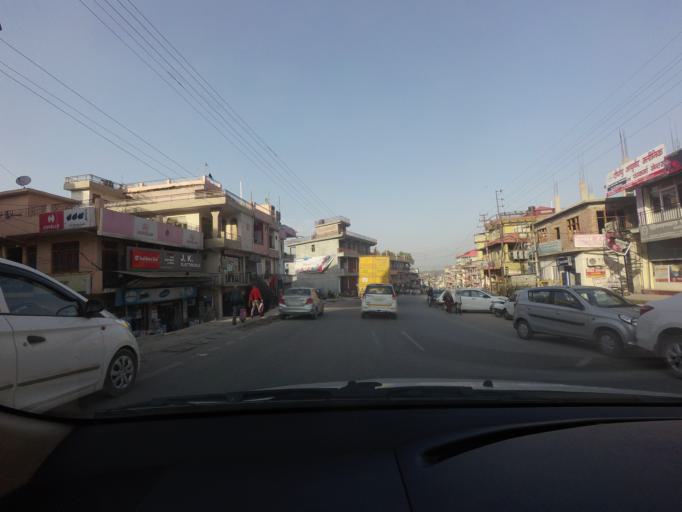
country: IN
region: Himachal Pradesh
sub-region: Mandi
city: Sundarnagar
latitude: 31.5321
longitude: 76.8881
